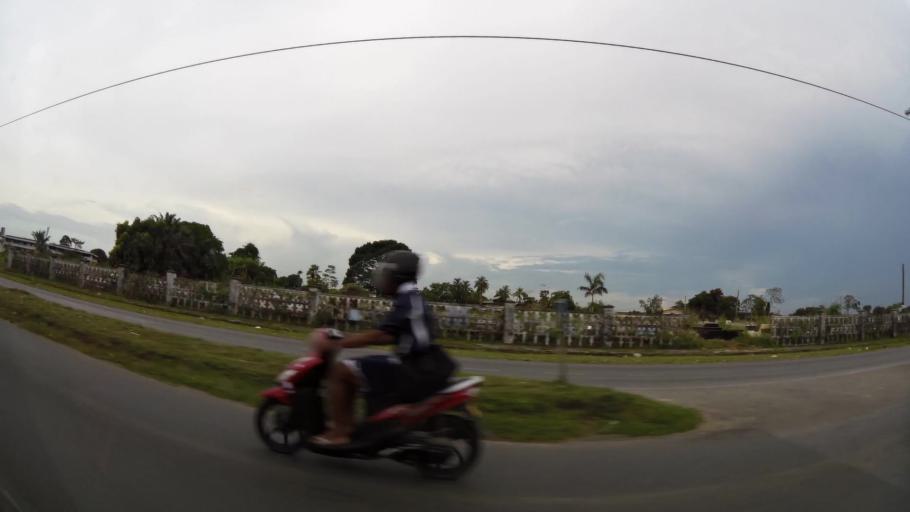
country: SR
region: Paramaribo
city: Paramaribo
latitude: 5.8155
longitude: -55.1932
